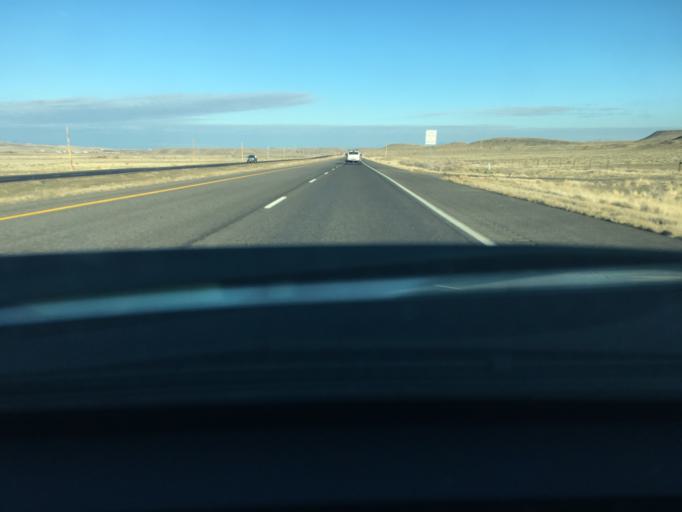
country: US
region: Colorado
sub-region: Mesa County
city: Clifton
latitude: 38.8999
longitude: -108.3665
